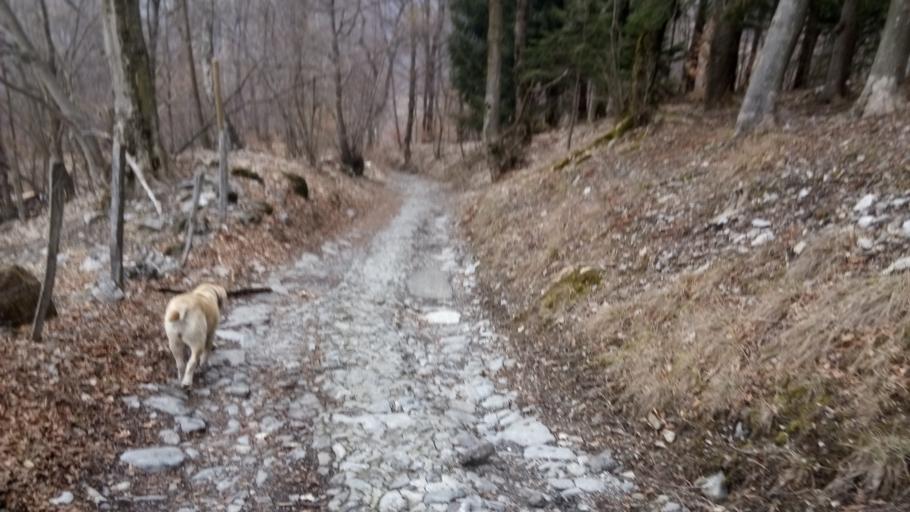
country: IT
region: Lombardy
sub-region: Provincia di Como
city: Occagno
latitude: 45.9124
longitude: 9.1004
